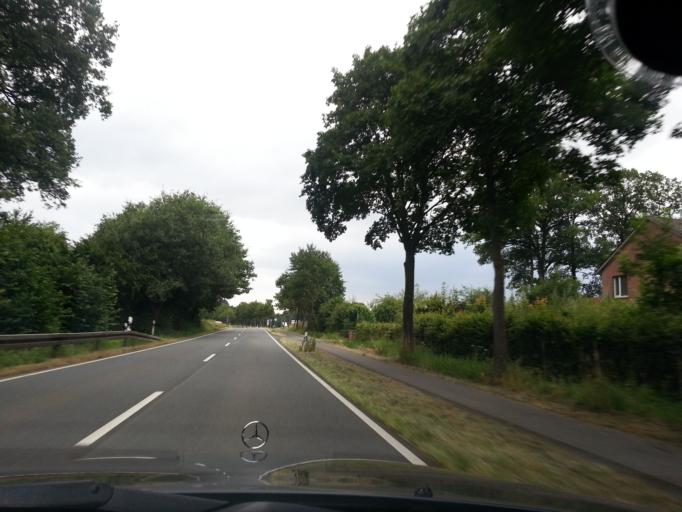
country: DE
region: North Rhine-Westphalia
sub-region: Regierungsbezirk Munster
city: Klein Reken
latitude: 51.7565
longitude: 7.0098
